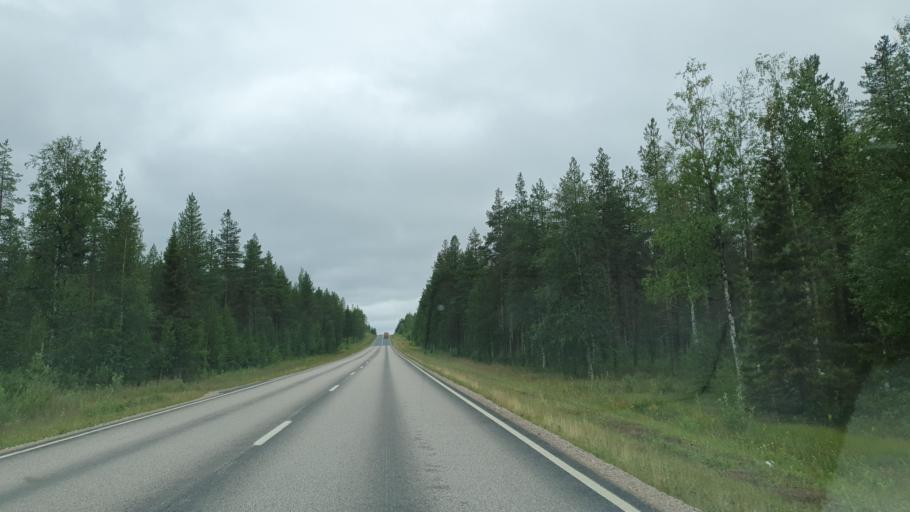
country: FI
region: Lapland
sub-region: Pohjois-Lappi
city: Sodankylae
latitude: 67.4142
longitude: 26.5089
